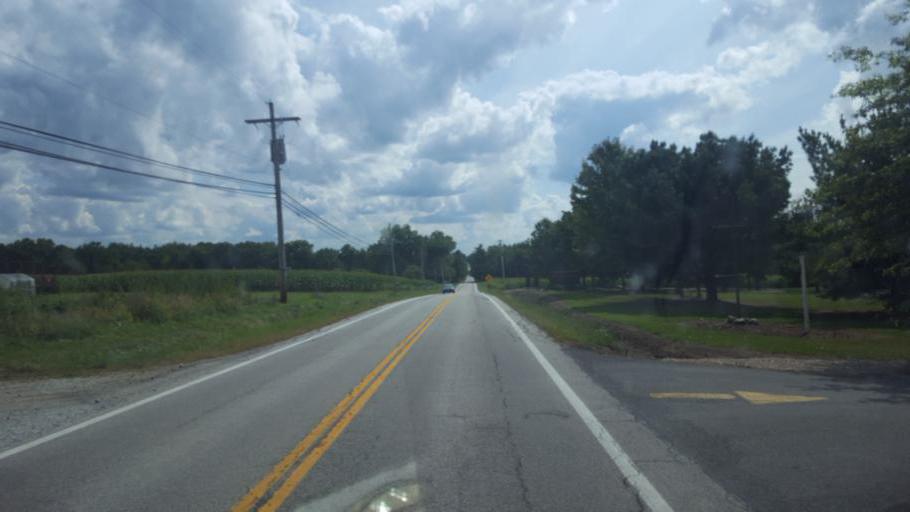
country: US
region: Ohio
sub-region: Portage County
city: Hiram
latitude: 41.3766
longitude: -81.1431
